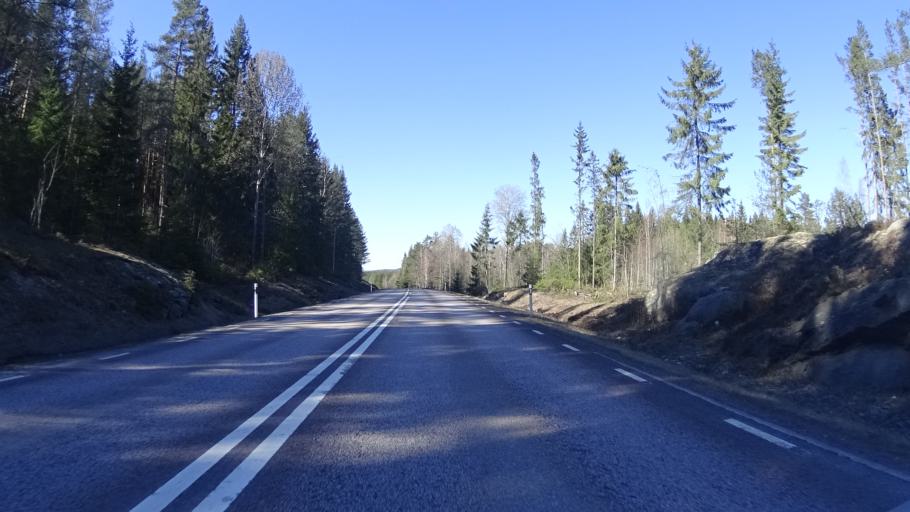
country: SE
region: Vaermland
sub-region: Karlstads Kommun
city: Edsvalla
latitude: 59.5946
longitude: 13.0077
